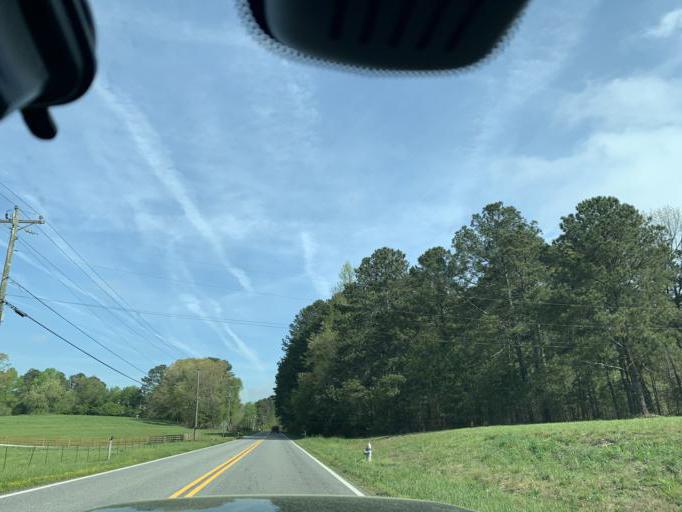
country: US
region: Georgia
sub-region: Forsyth County
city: Cumming
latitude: 34.2190
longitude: -84.0837
